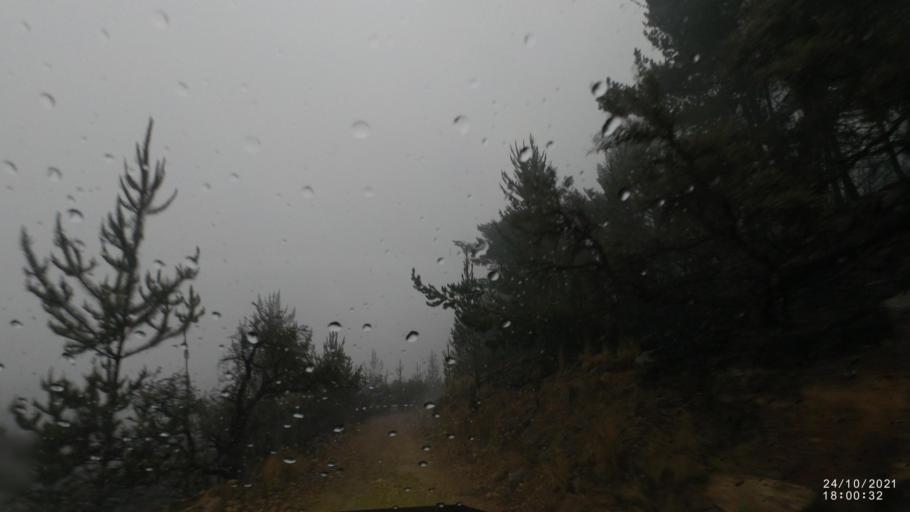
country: BO
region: Cochabamba
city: Cochabamba
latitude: -17.3260
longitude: -66.1292
